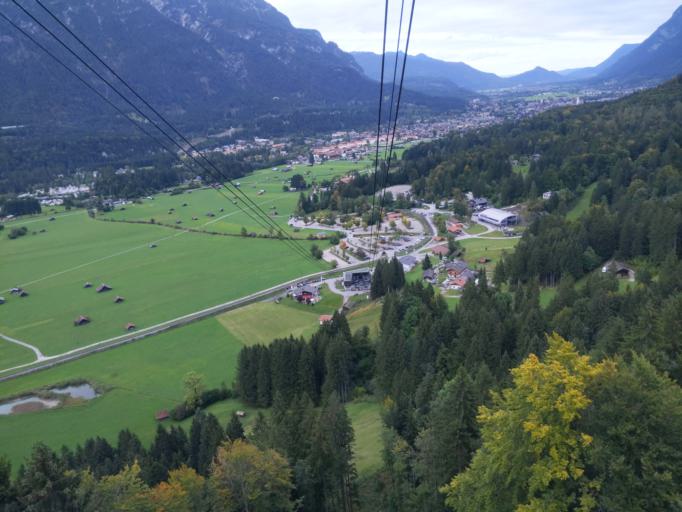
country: DE
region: Bavaria
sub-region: Upper Bavaria
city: Grainau
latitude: 47.4668
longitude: 11.0601
